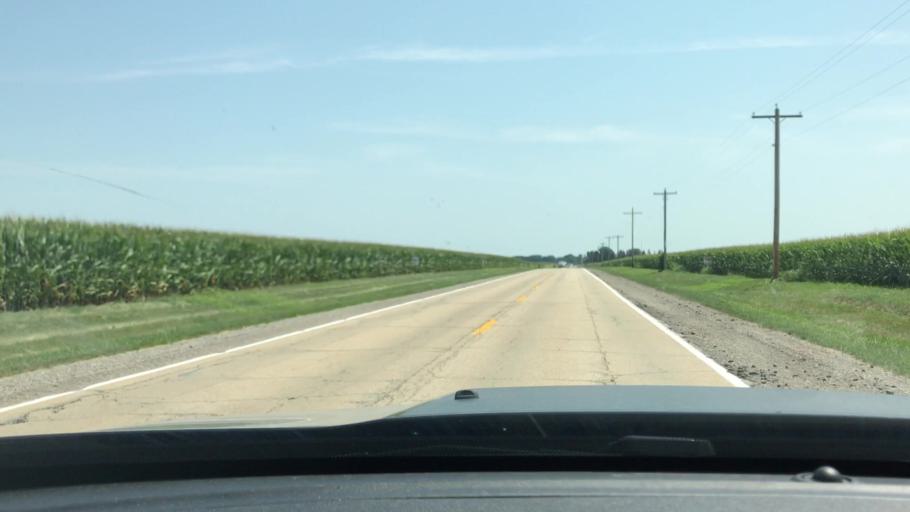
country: US
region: Illinois
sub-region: LaSalle County
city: Sheridan
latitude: 41.4853
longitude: -88.7953
